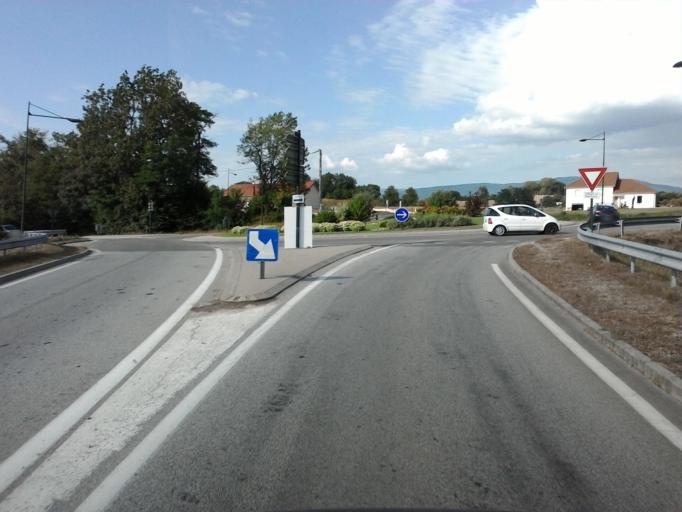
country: FR
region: Rhone-Alpes
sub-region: Departement de l'Isere
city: Morestel
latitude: 45.6866
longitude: 5.4606
